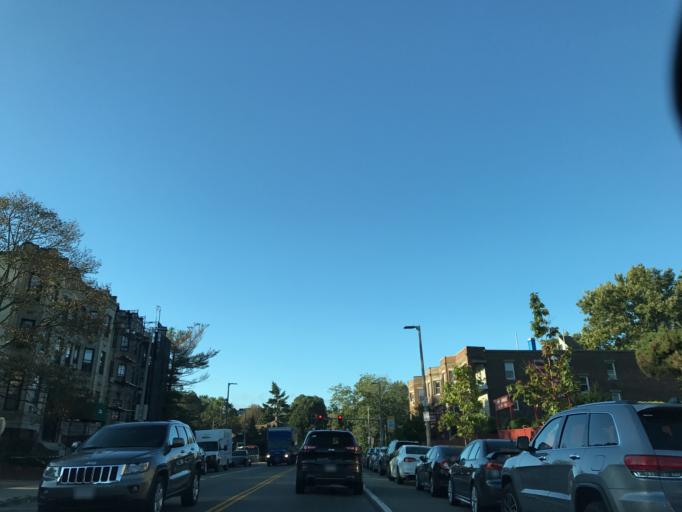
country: US
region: Massachusetts
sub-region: Norfolk County
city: Brookline
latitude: 42.3412
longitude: -71.1549
